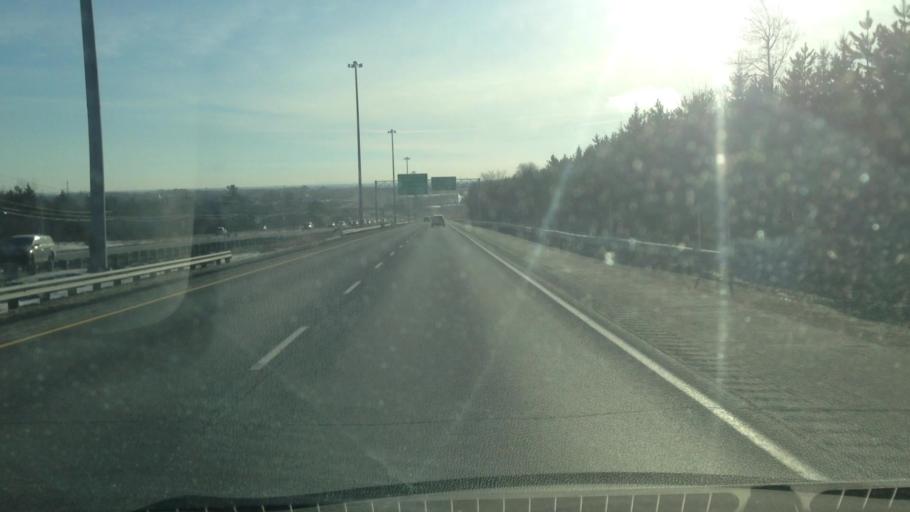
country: CA
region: Quebec
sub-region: Laurentides
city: Saint-Jerome
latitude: 45.8026
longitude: -74.0339
